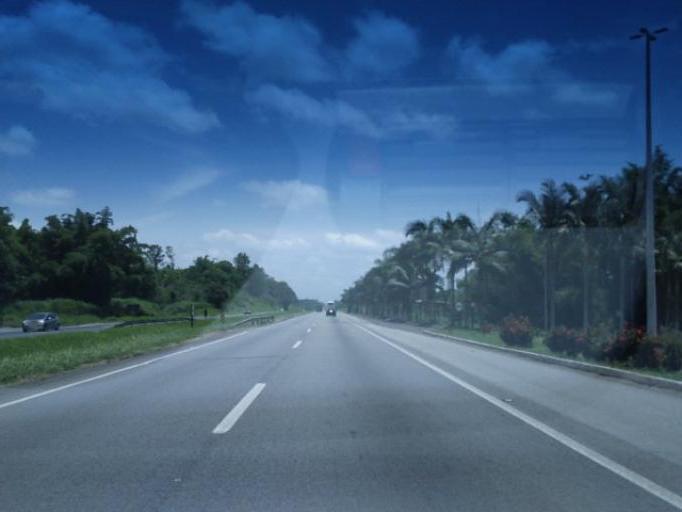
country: BR
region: Sao Paulo
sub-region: Registro
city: Registro
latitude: -24.4243
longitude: -47.7799
